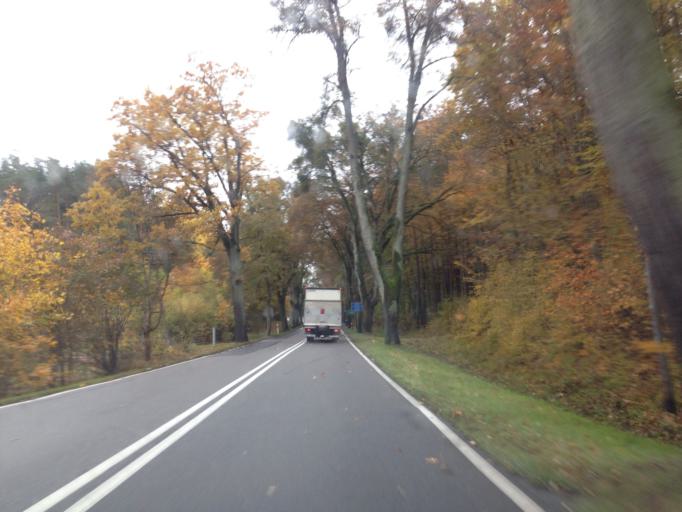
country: PL
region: Pomeranian Voivodeship
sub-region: Powiat kwidzynski
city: Ryjewo
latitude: 53.8578
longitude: 19.0010
